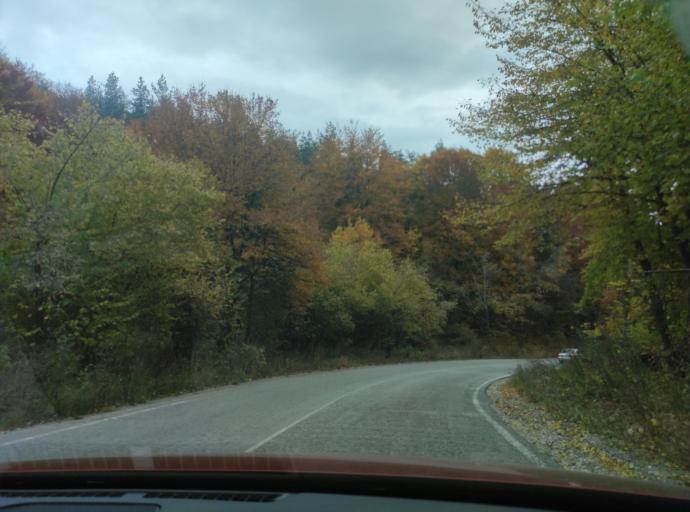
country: BG
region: Sofiya
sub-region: Obshtina Godech
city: Godech
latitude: 43.0211
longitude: 23.1355
